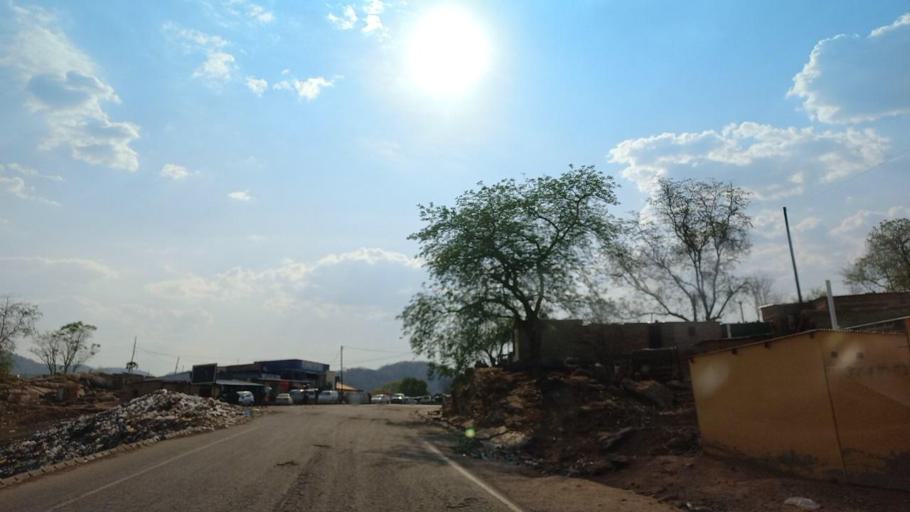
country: ZM
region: Lusaka
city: Luangwa
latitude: -14.9851
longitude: 30.2060
